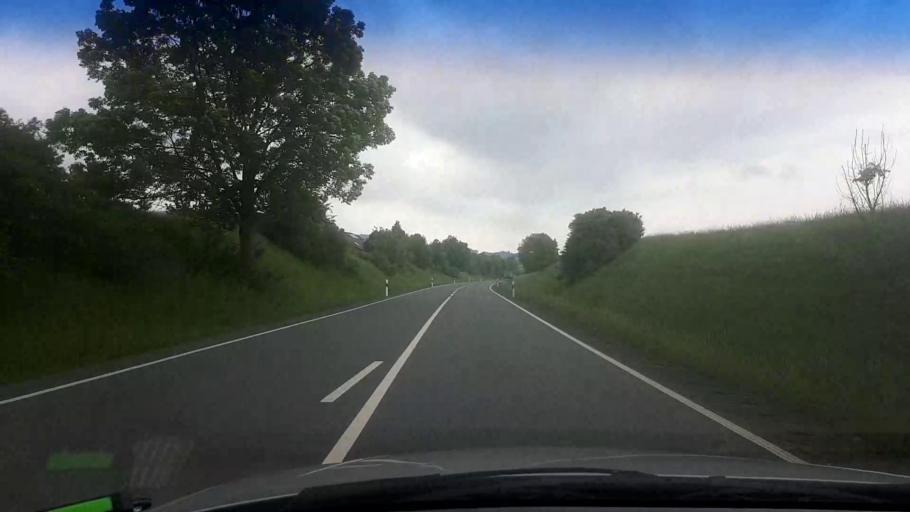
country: DE
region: Bavaria
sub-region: Upper Franconia
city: Goldkronach
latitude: 50.0084
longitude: 11.6771
